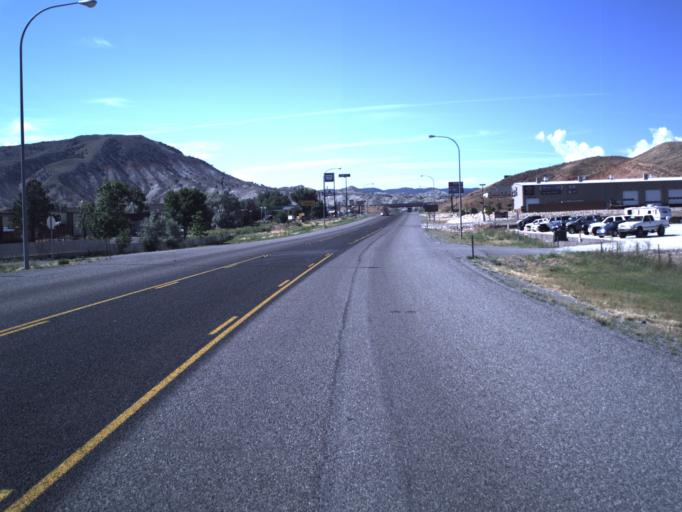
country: US
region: Utah
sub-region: Sevier County
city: Salina
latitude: 38.9423
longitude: -111.8547
